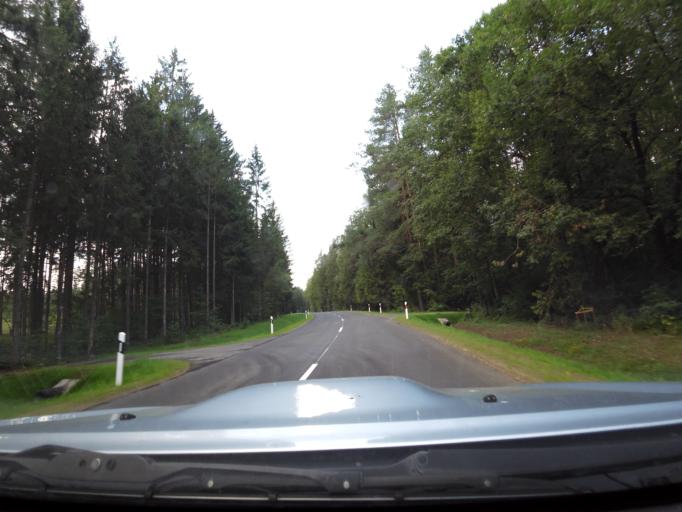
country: LT
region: Vilnius County
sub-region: Vilniaus Rajonas
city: Vievis
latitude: 54.8764
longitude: 24.8054
